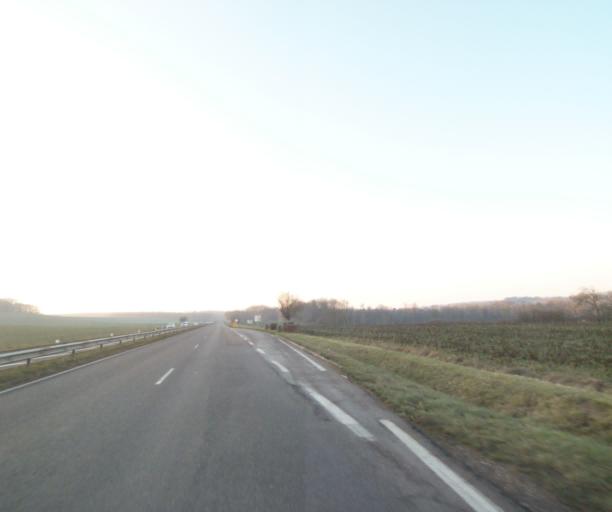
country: FR
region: Lorraine
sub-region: Departement de la Meuse
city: Ancerville
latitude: 48.6073
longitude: 5.0196
